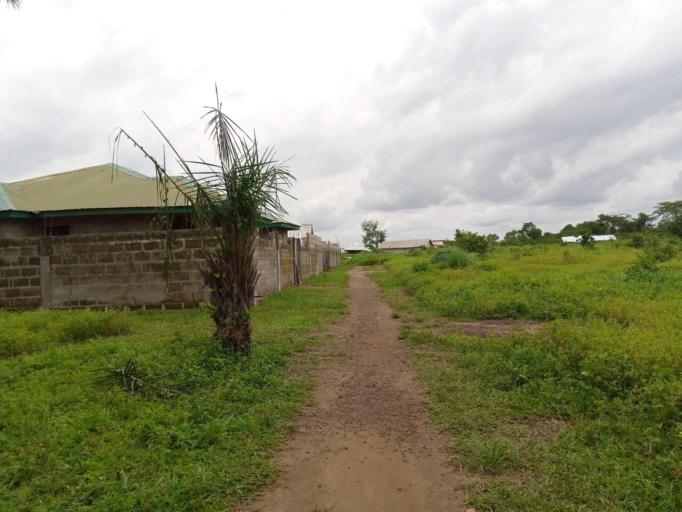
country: SL
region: Southern Province
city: Moyamba
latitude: 8.1622
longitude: -12.4242
